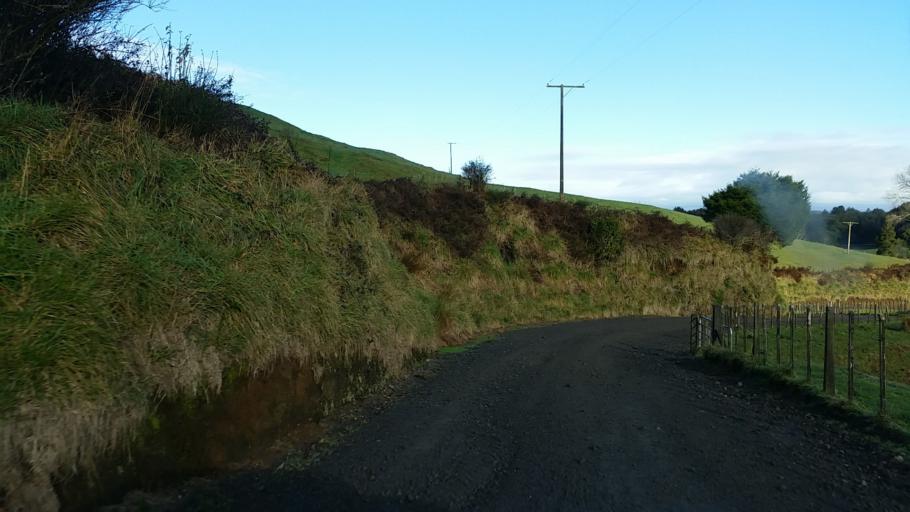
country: NZ
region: Taranaki
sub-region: South Taranaki District
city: Eltham
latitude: -39.2477
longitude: 174.3802
